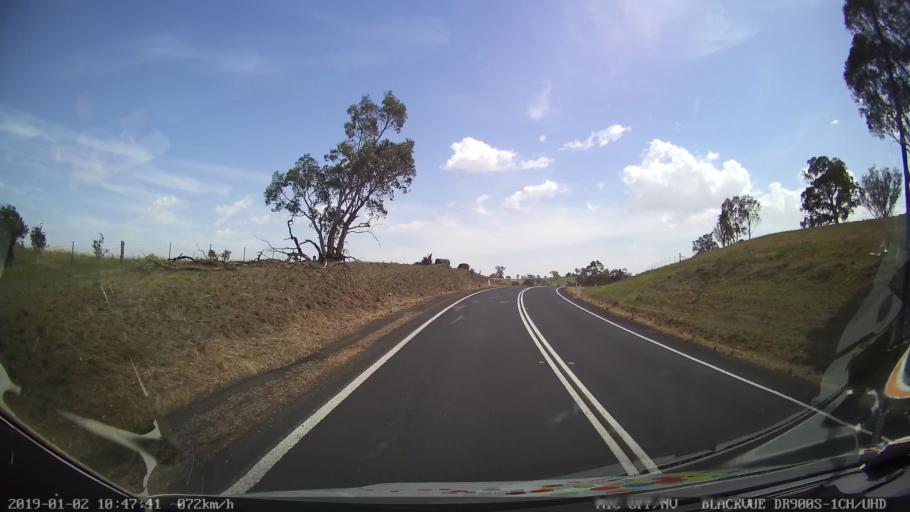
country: AU
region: New South Wales
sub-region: Cootamundra
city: Cootamundra
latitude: -34.7424
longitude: 148.2718
